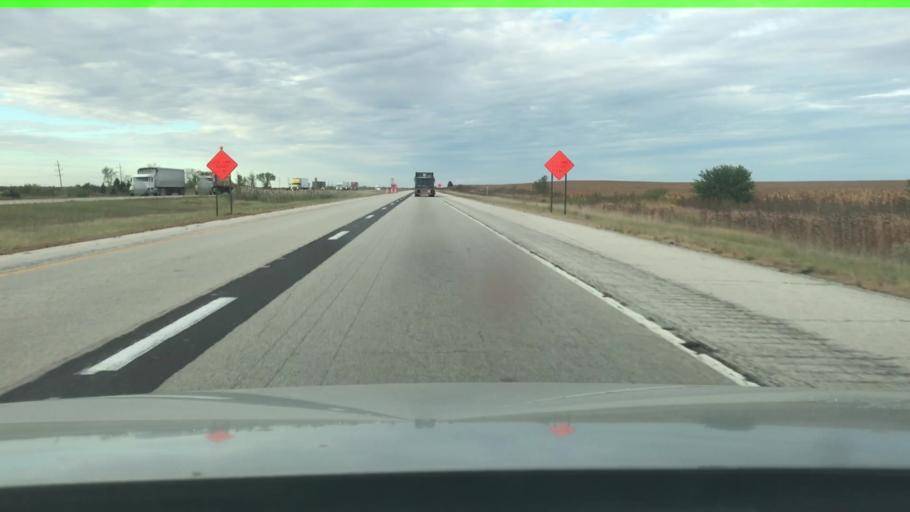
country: US
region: Illinois
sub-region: Livingston County
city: Odell
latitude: 40.9693
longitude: -88.5580
